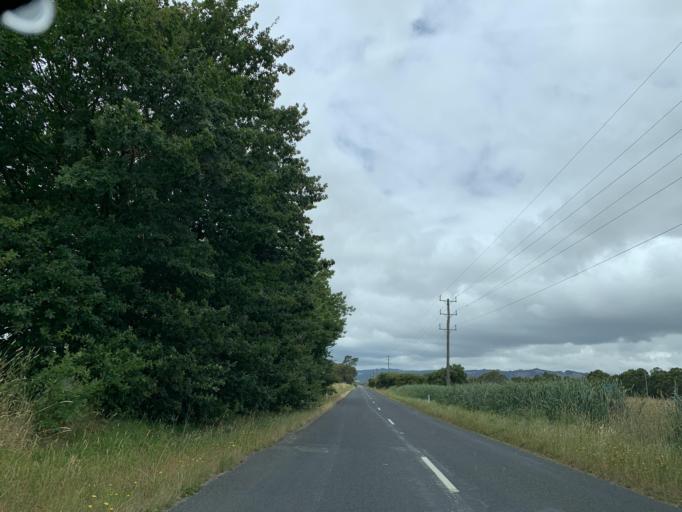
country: AU
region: Victoria
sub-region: Latrobe
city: Moe
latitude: -38.2062
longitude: 146.1033
